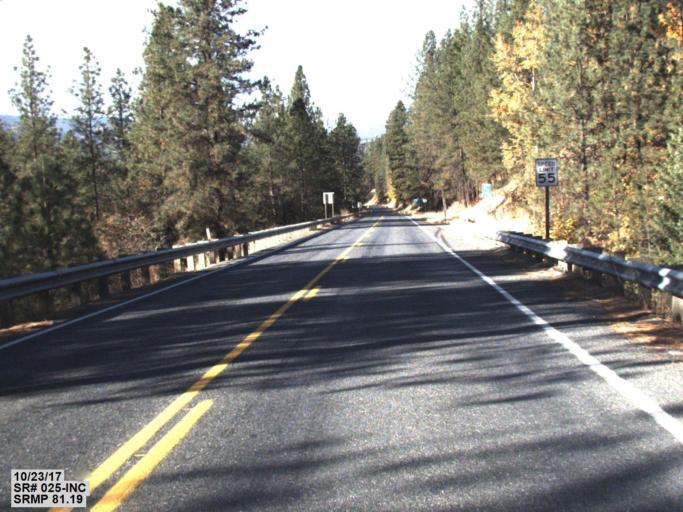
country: US
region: Washington
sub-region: Stevens County
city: Kettle Falls
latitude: 48.6080
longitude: -118.0755
